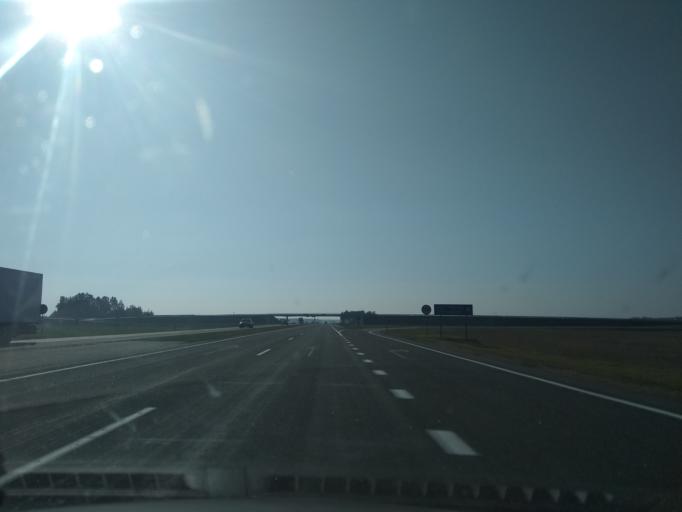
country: BY
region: Brest
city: Antopal'
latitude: 52.3097
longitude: 24.6008
